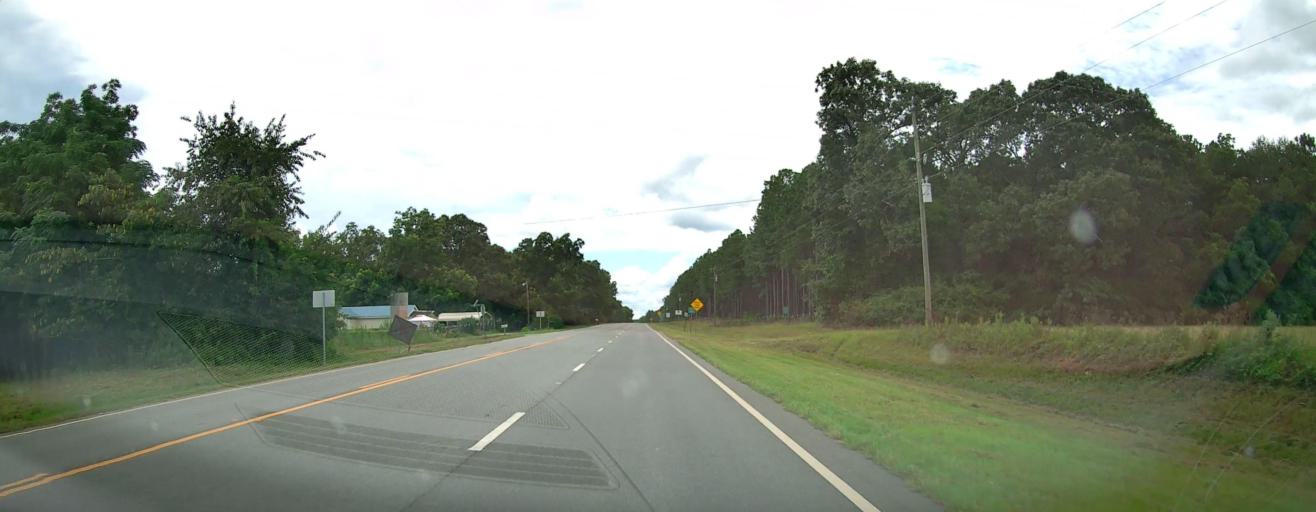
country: US
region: Georgia
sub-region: Schley County
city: Ellaville
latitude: 32.2599
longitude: -84.2188
